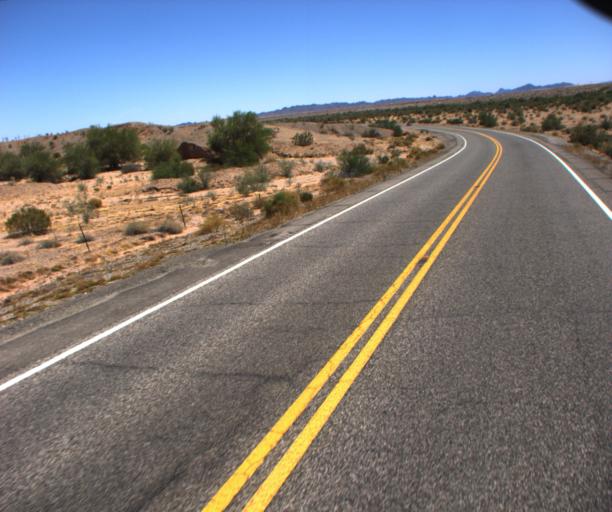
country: US
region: Arizona
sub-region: La Paz County
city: Parker
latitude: 34.0000
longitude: -114.2295
